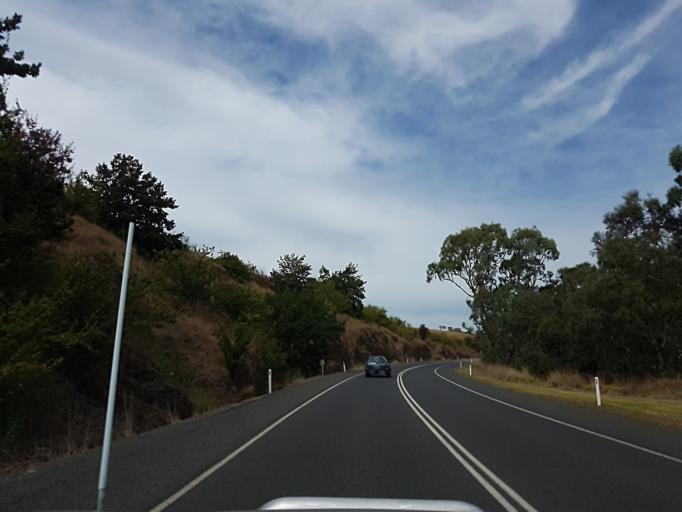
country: AU
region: Victoria
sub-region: Murrindindi
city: Alexandra
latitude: -37.2096
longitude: 145.4351
